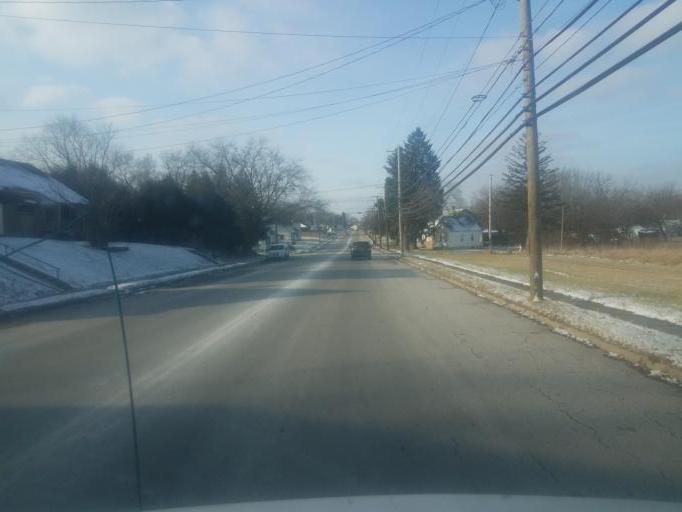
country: US
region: Ohio
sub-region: Richland County
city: Mansfield
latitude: 40.7465
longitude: -82.5058
